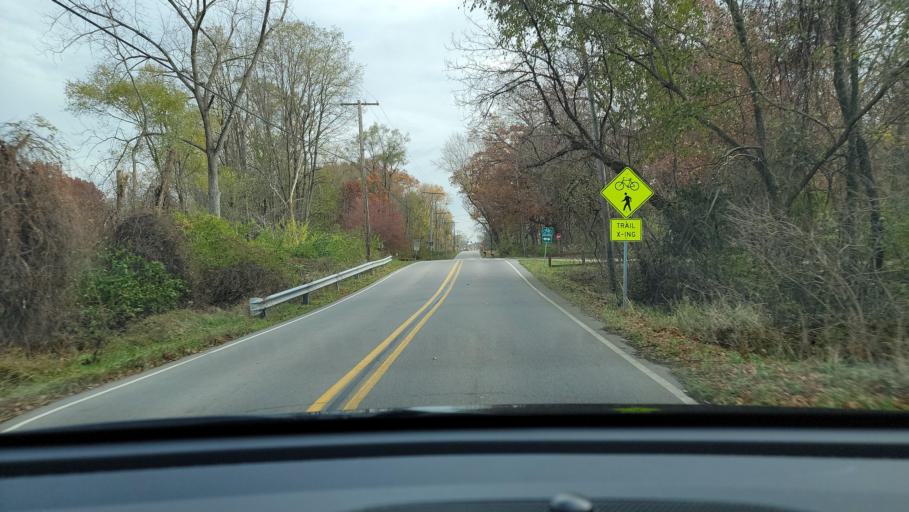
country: US
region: Indiana
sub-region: Porter County
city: Burns Harbor
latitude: 41.5865
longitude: -87.1303
